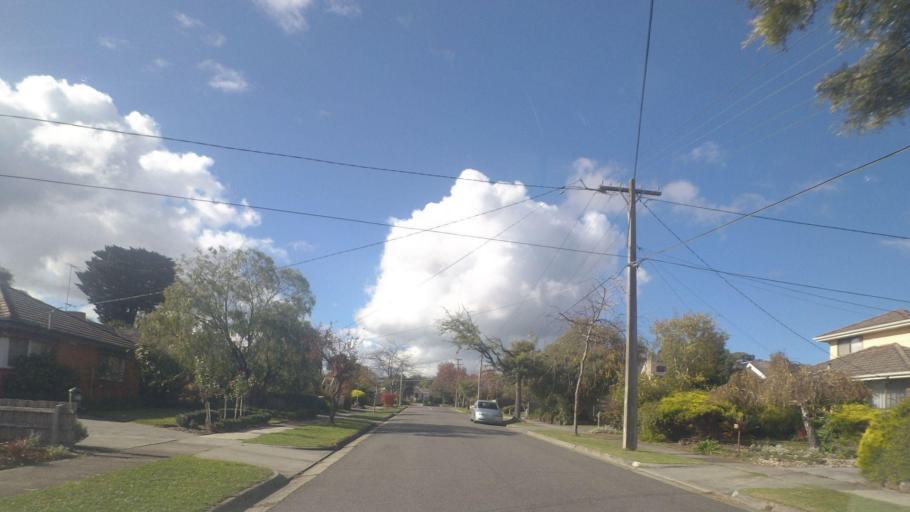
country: AU
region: Victoria
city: Forest Hill
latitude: -37.8397
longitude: 145.1840
